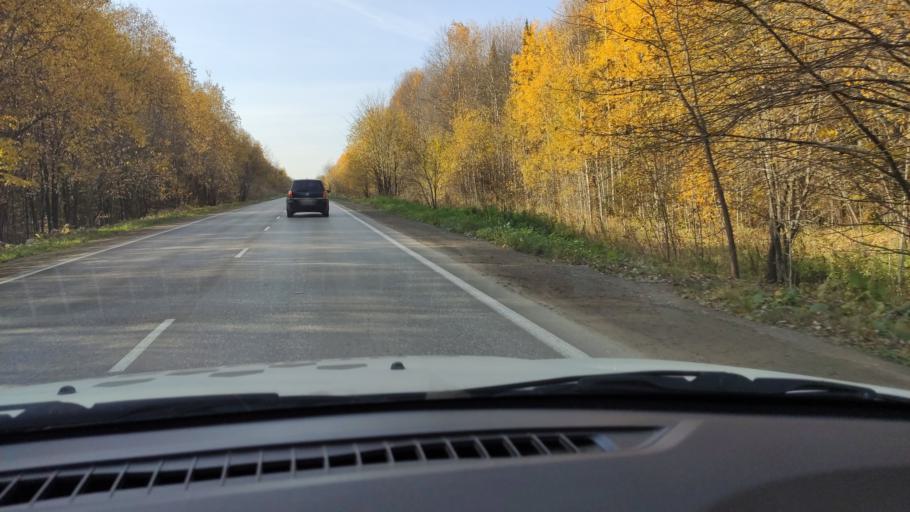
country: RU
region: Perm
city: Novyye Lyady
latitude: 58.0212
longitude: 56.6540
